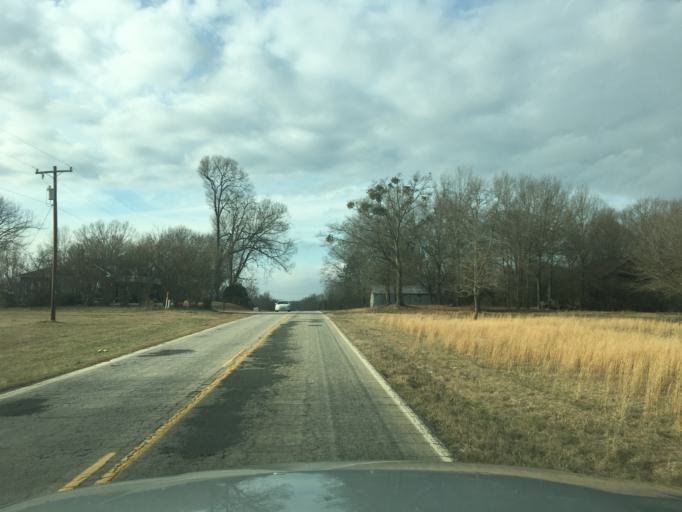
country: US
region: South Carolina
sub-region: Abbeville County
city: Due West
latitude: 34.3444
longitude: -82.4948
